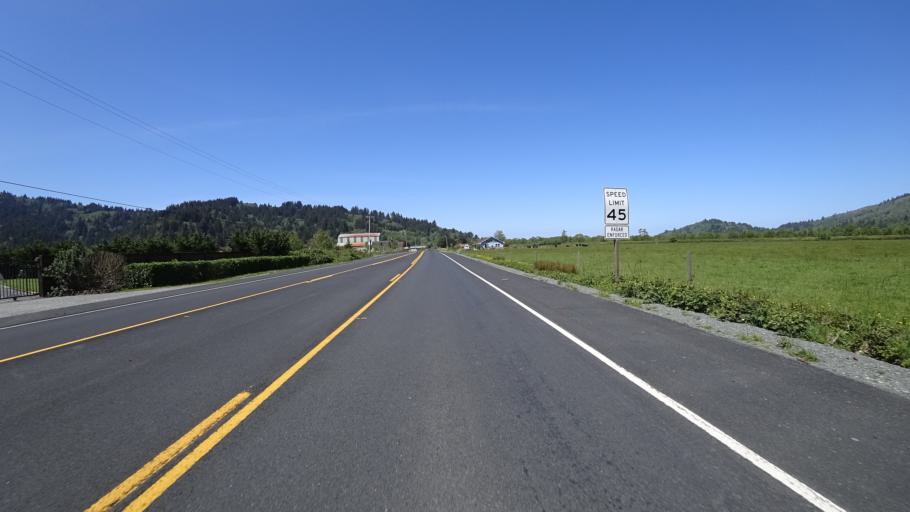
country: US
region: California
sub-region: Humboldt County
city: Westhaven-Moonstone
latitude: 41.2846
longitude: -124.0640
